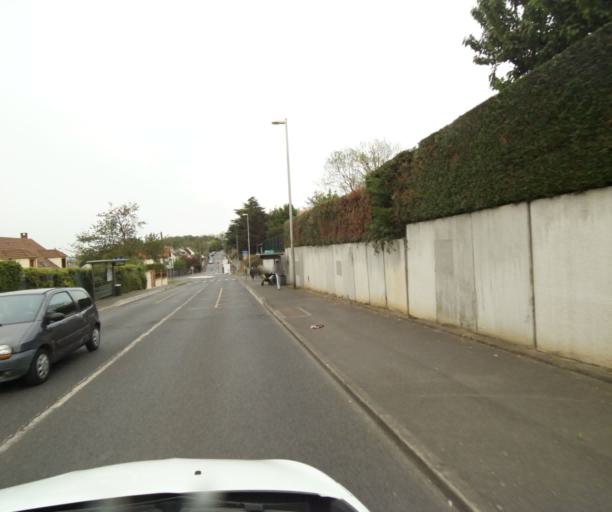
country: FR
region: Ile-de-France
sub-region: Departement de Seine-et-Marne
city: Torcy
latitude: 48.8548
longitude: 2.6398
